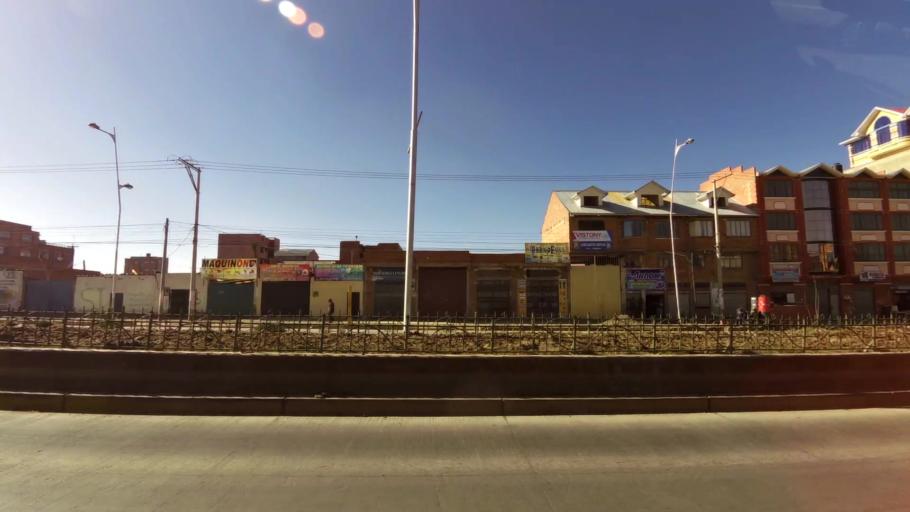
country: BO
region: La Paz
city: La Paz
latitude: -16.5291
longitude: -68.1855
